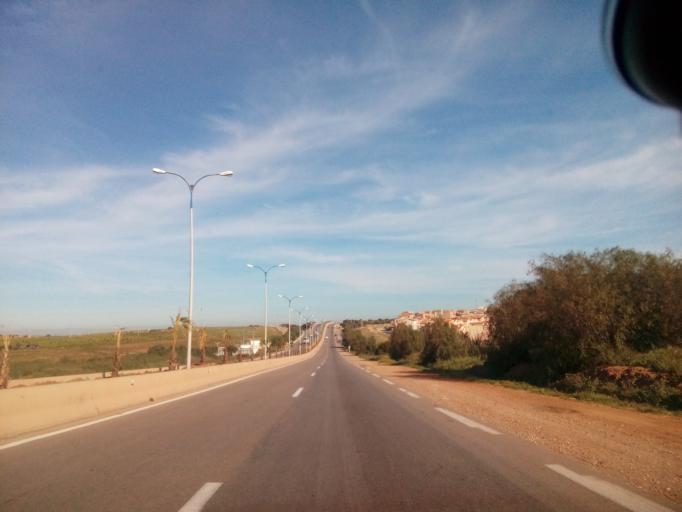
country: DZ
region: Mostaganem
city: Mostaganem
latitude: 35.8272
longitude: -0.0117
